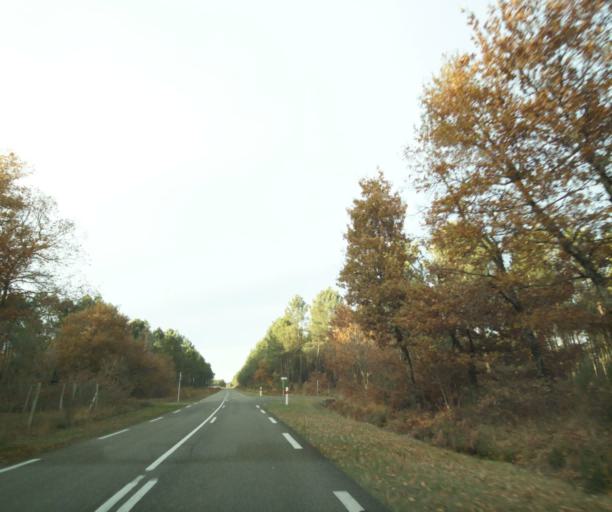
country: FR
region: Aquitaine
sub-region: Departement des Landes
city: Gabarret
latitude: 44.1552
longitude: -0.1307
